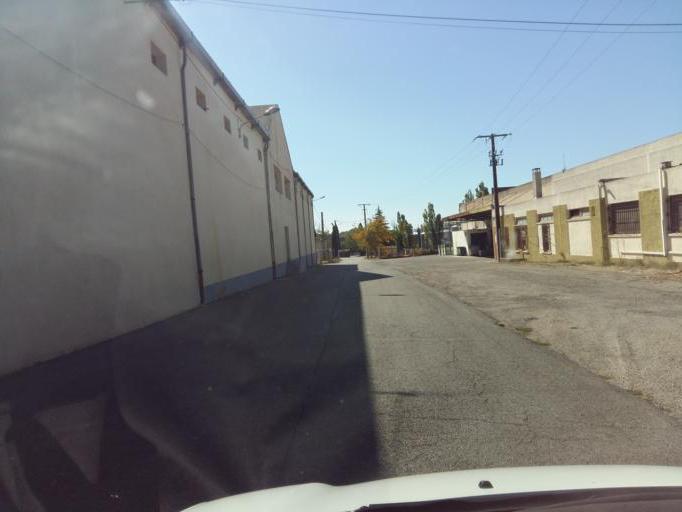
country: FR
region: Provence-Alpes-Cote d'Azur
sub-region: Departement du Vaucluse
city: Pertuis
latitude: 43.7217
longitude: 5.5444
